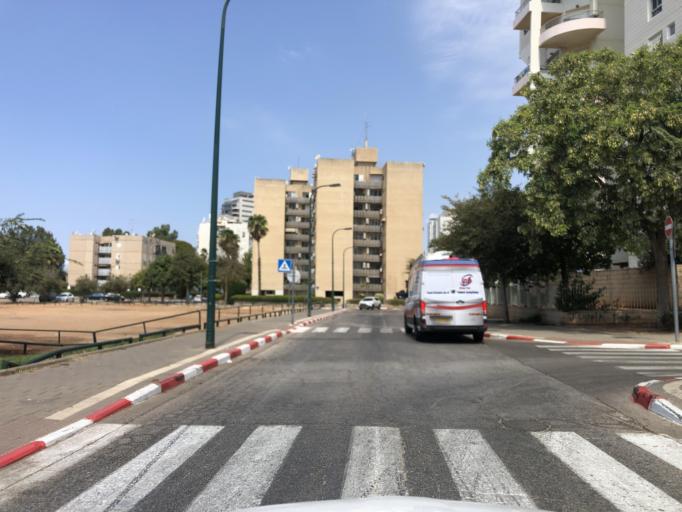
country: IL
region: Tel Aviv
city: Azor
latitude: 32.0438
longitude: 34.8002
